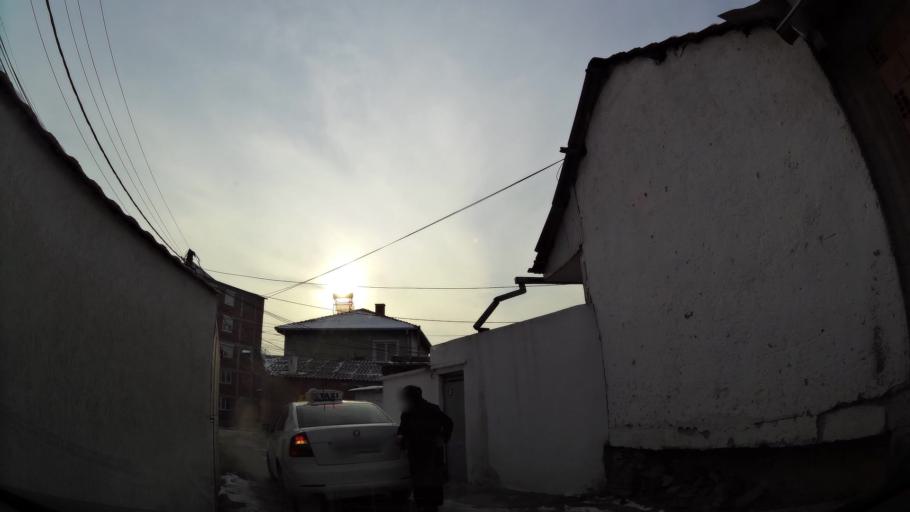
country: MK
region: Cair
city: Cair
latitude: 42.0174
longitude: 21.4392
